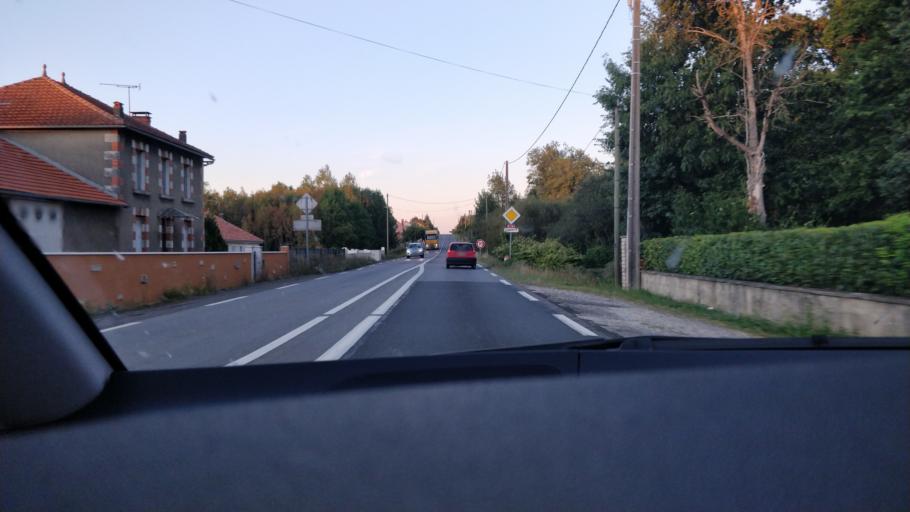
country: FR
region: Poitou-Charentes
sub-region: Departement de la Charente
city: Loubert
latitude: 45.8678
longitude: 0.5451
